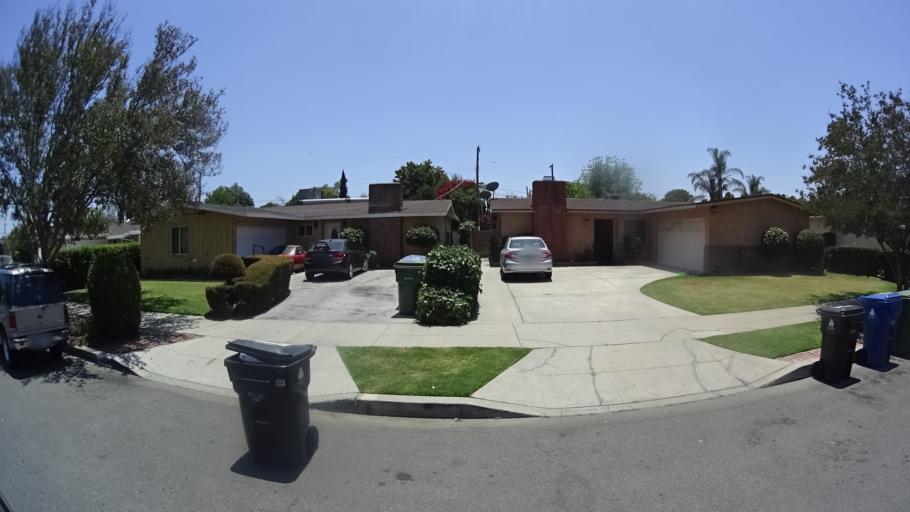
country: US
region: California
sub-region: Los Angeles County
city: Van Nuys
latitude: 34.2171
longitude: -118.4566
